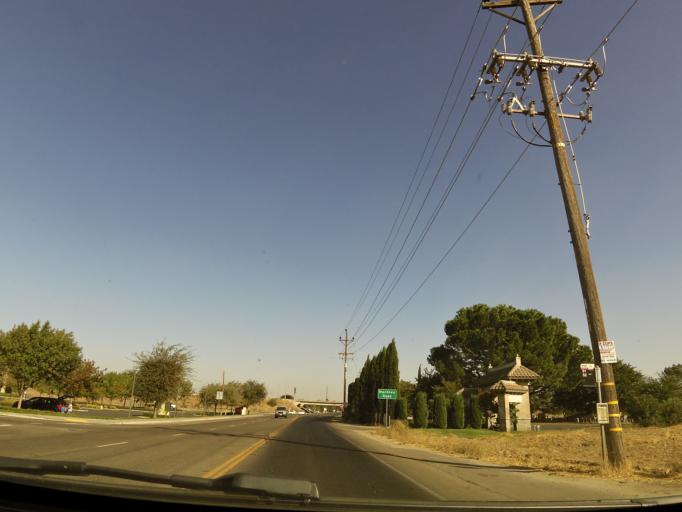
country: US
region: California
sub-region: San Joaquin County
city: French Camp
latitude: 37.8823
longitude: -121.2823
